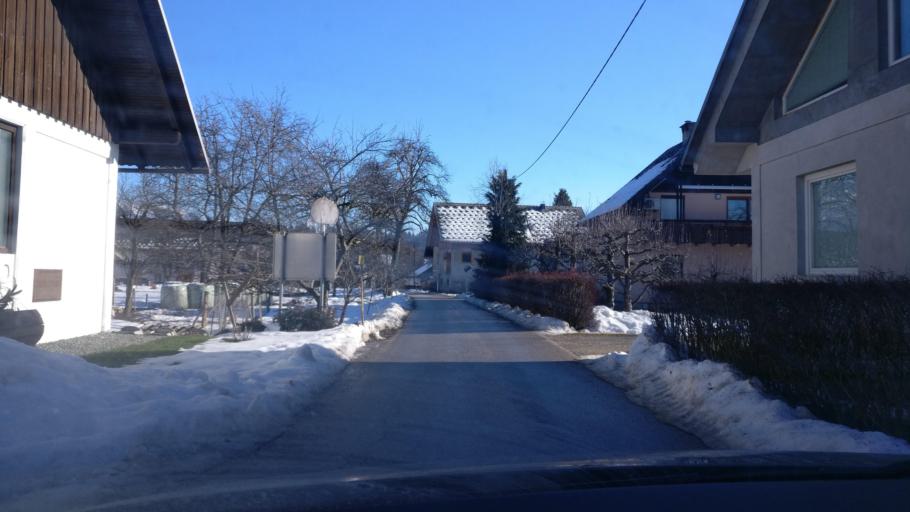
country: SI
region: Radovljica
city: Radovljica
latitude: 46.3276
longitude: 14.2327
